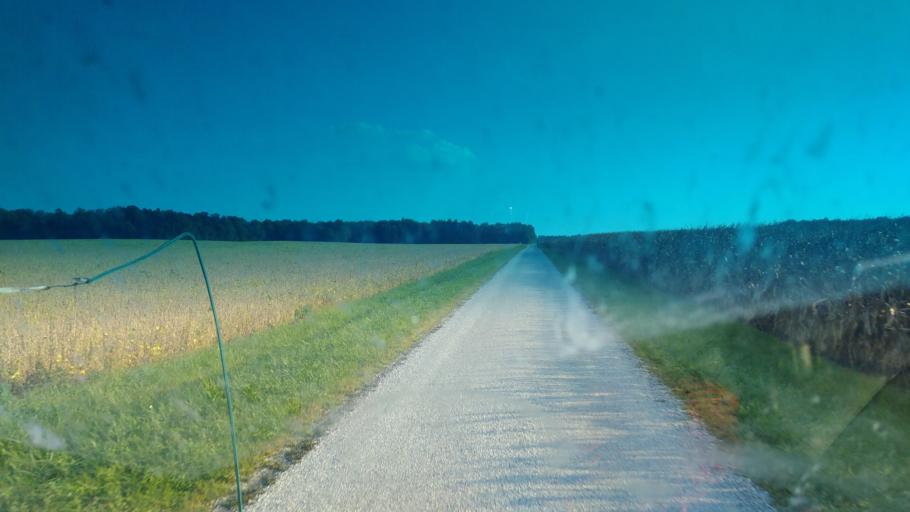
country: US
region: Ohio
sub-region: Crawford County
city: Bucyrus
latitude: 40.9353
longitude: -82.9973
